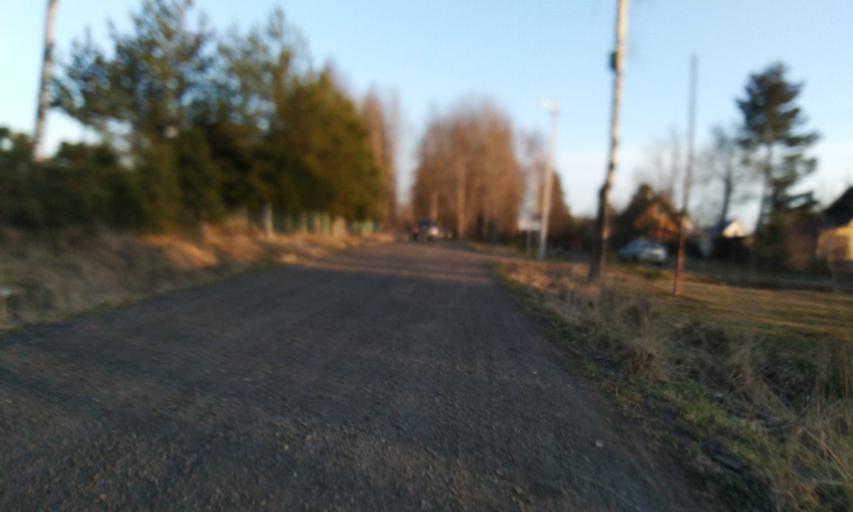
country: RU
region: Leningrad
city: Novoye Devyatkino
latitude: 60.0880
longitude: 30.4570
